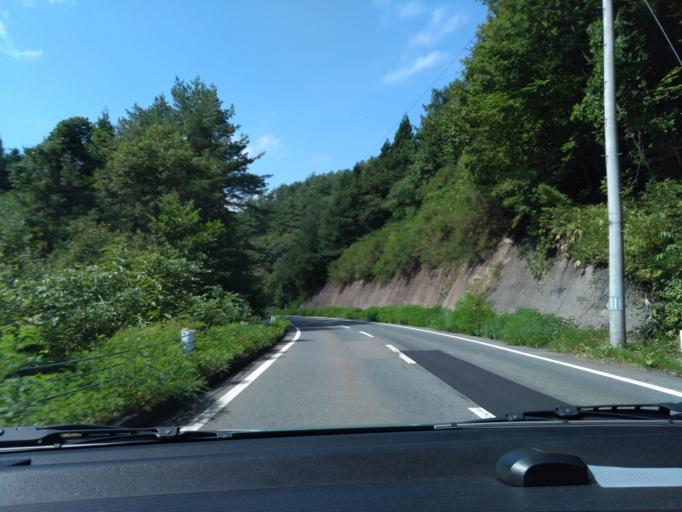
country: JP
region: Iwate
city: Shizukuishi
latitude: 39.6391
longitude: 141.0160
